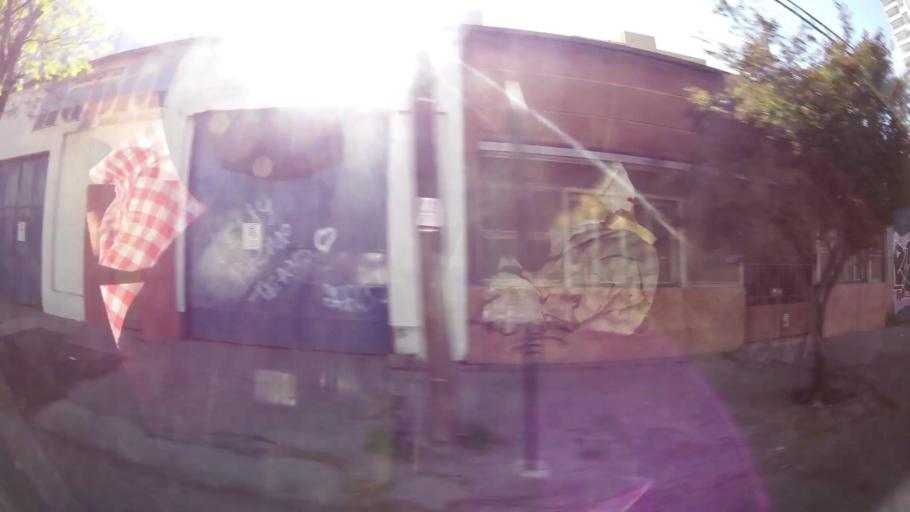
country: CL
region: Santiago Metropolitan
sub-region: Provincia de Santiago
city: Santiago
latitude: -33.4538
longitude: -70.6317
